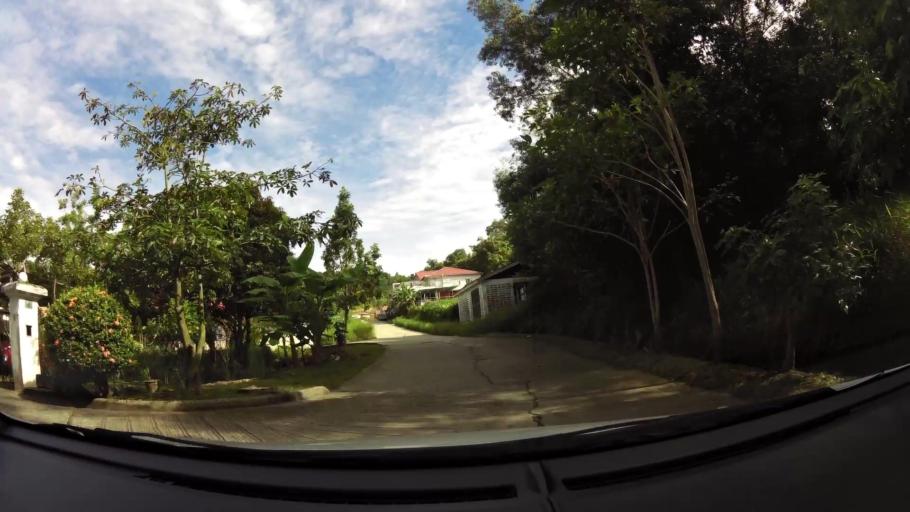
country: BN
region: Brunei and Muara
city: Bandar Seri Begawan
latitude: 4.9020
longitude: 114.9707
